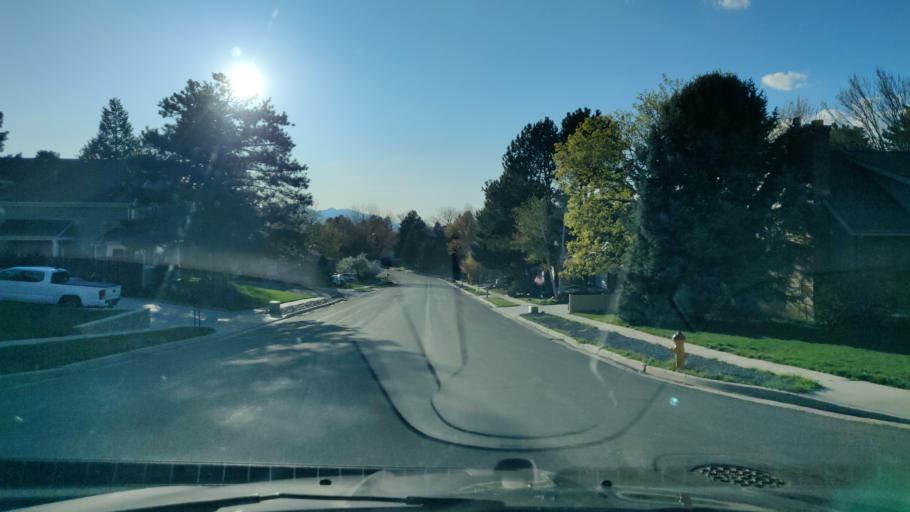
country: US
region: Utah
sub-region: Salt Lake County
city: Cottonwood Heights
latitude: 40.6142
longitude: -111.7932
